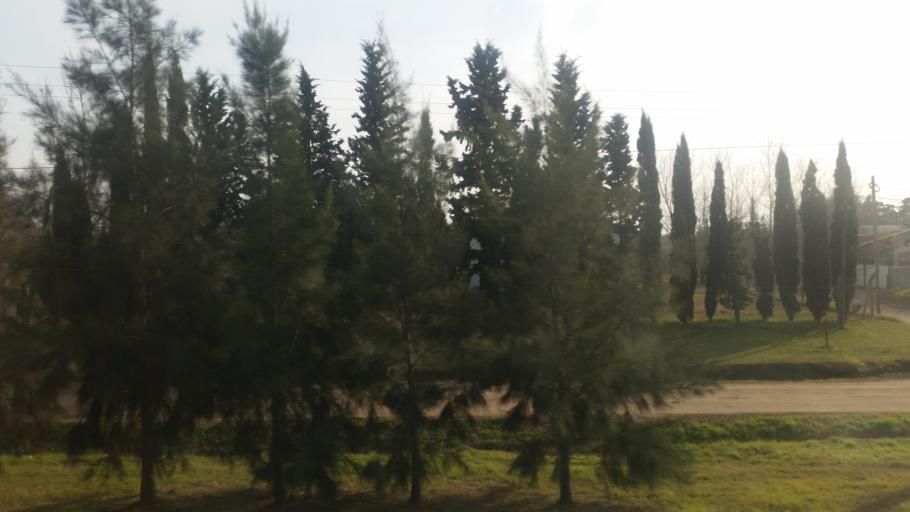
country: AR
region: Cordoba
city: Bell Ville
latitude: -32.6103
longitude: -62.6825
